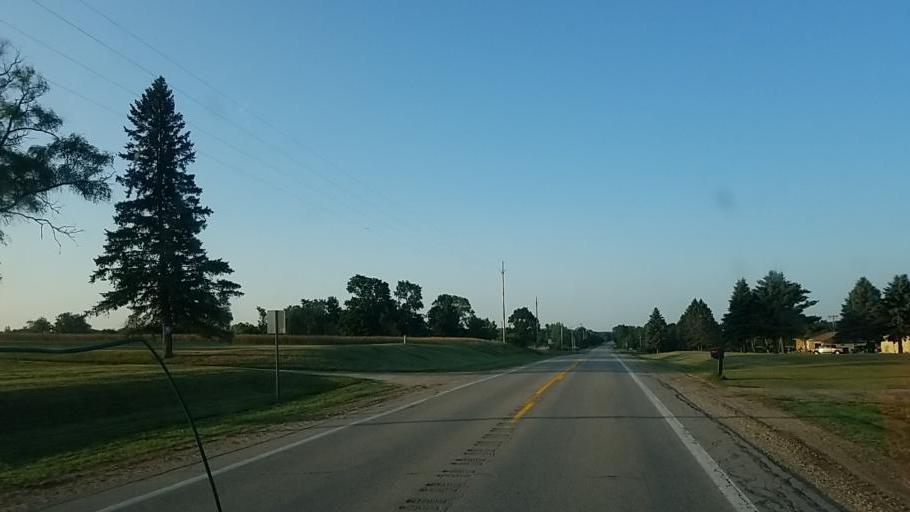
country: US
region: Michigan
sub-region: Isabella County
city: Lake Isabella
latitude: 43.6163
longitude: -85.1457
